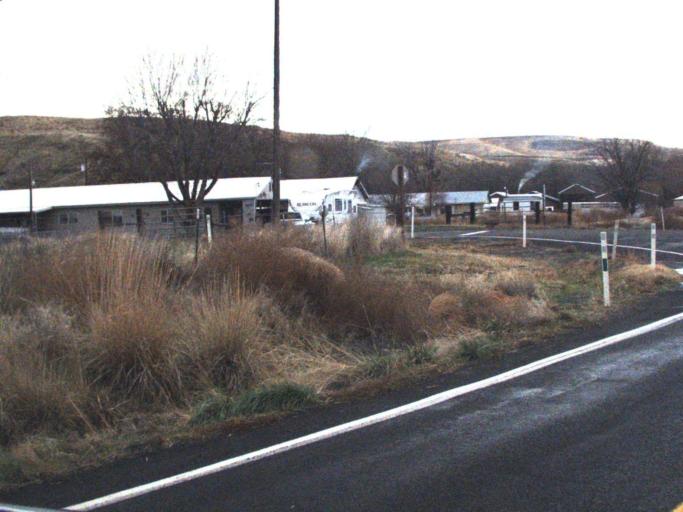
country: US
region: Washington
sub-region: Columbia County
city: Dayton
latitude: 46.5217
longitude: -118.1276
